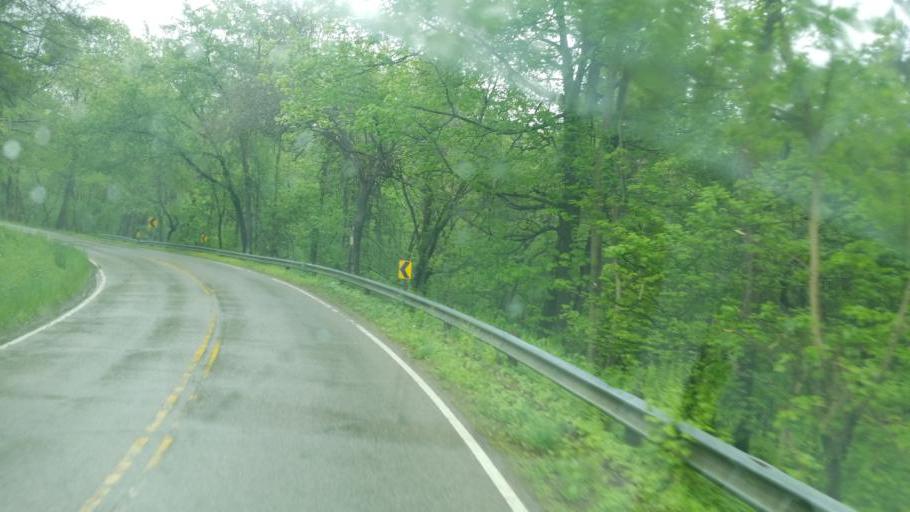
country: US
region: Ohio
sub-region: Muskingum County
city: Frazeysburg
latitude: 40.1011
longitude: -82.1064
